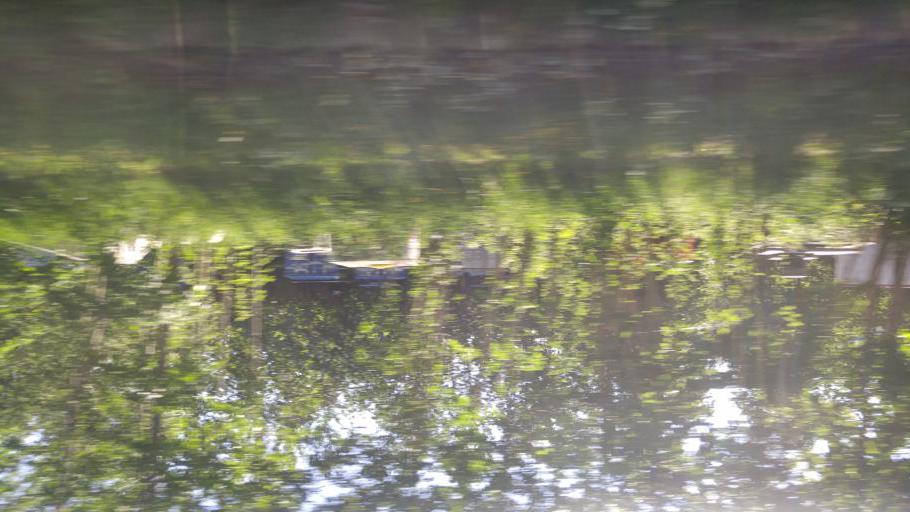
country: NO
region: Sor-Trondelag
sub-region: Melhus
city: Melhus
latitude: 63.2598
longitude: 10.2878
